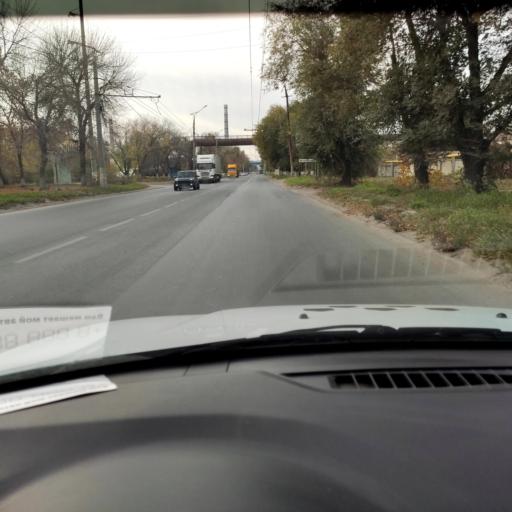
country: RU
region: Samara
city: Tol'yatti
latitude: 53.5603
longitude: 49.4539
